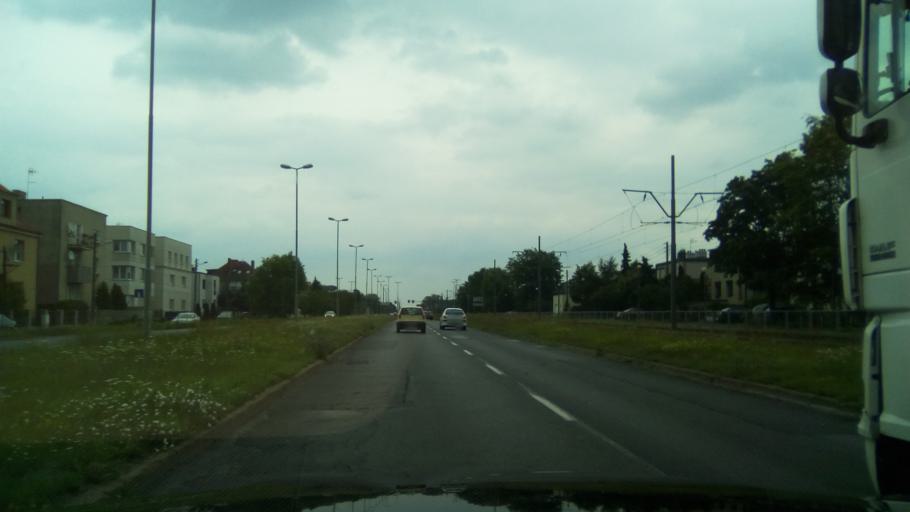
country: PL
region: Greater Poland Voivodeship
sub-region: Powiat poznanski
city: Czerwonak
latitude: 52.4098
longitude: 16.9866
